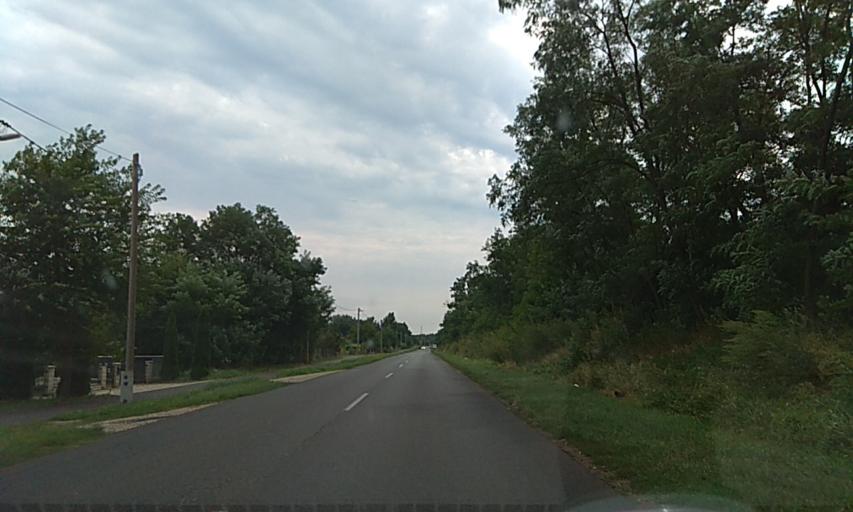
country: HU
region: Szabolcs-Szatmar-Bereg
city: Nyiregyhaza
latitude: 47.9960
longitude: 21.7026
